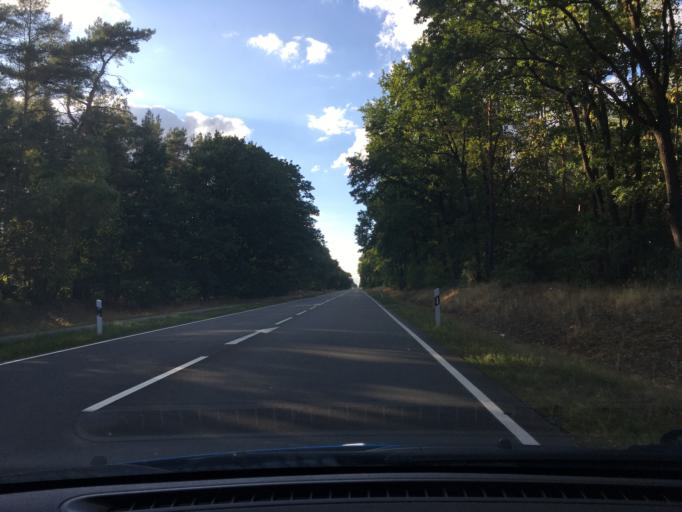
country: DE
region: Mecklenburg-Vorpommern
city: Grabow
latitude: 53.2915
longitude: 11.5448
